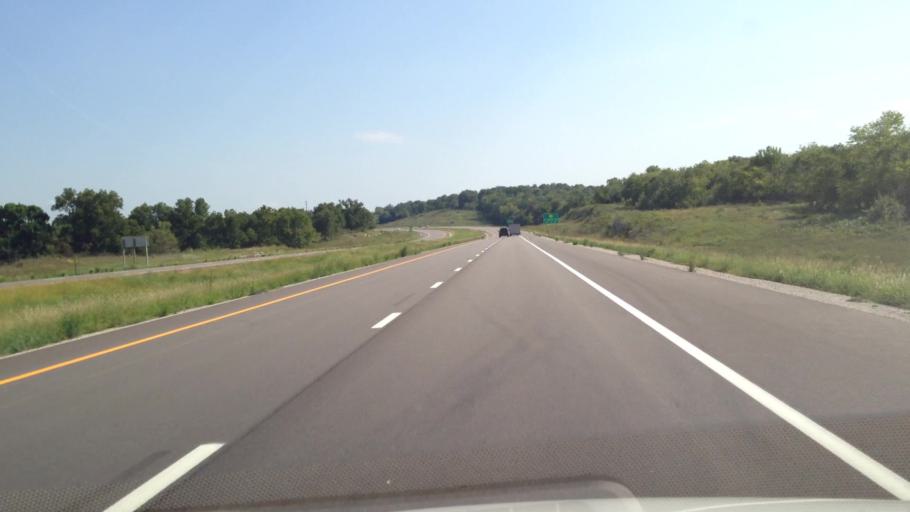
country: US
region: Kansas
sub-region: Linn County
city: La Cygne
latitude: 38.3604
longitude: -94.6876
